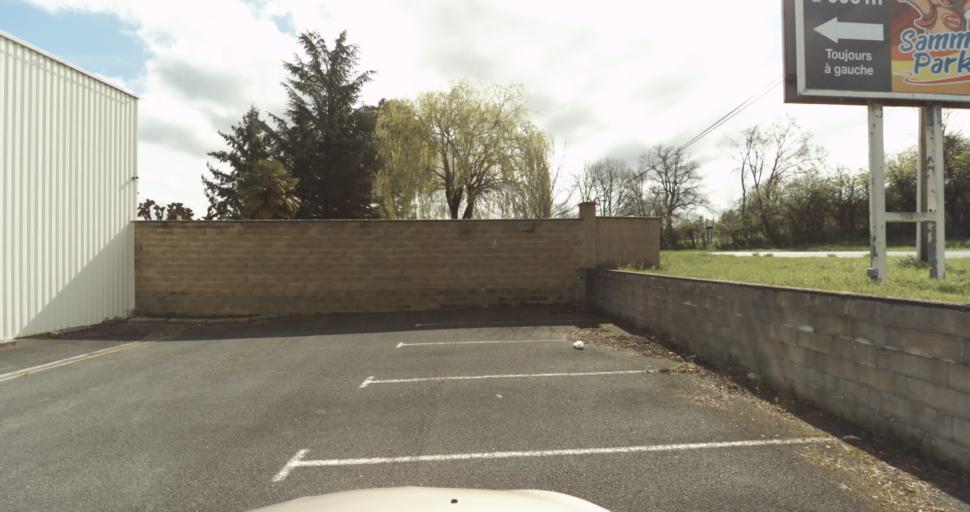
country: FR
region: Midi-Pyrenees
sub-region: Departement du Tarn
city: Puygouzon
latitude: 43.8918
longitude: 2.1571
